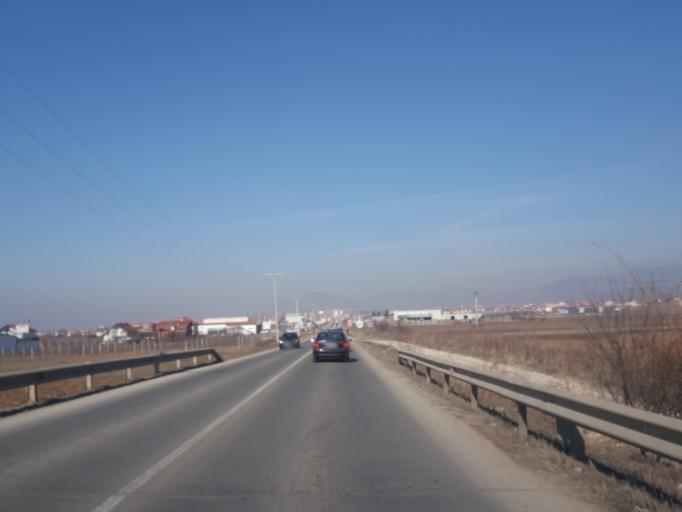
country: XK
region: Mitrovica
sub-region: Vushtrri
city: Vushtrri
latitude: 42.8035
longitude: 20.9927
